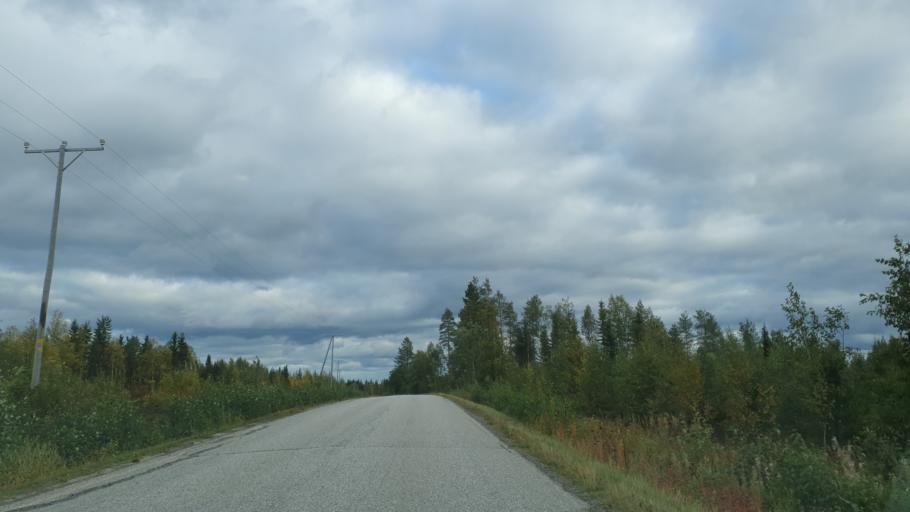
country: FI
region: Kainuu
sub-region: Kehys-Kainuu
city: Kuhmo
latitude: 63.9539
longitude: 29.7377
